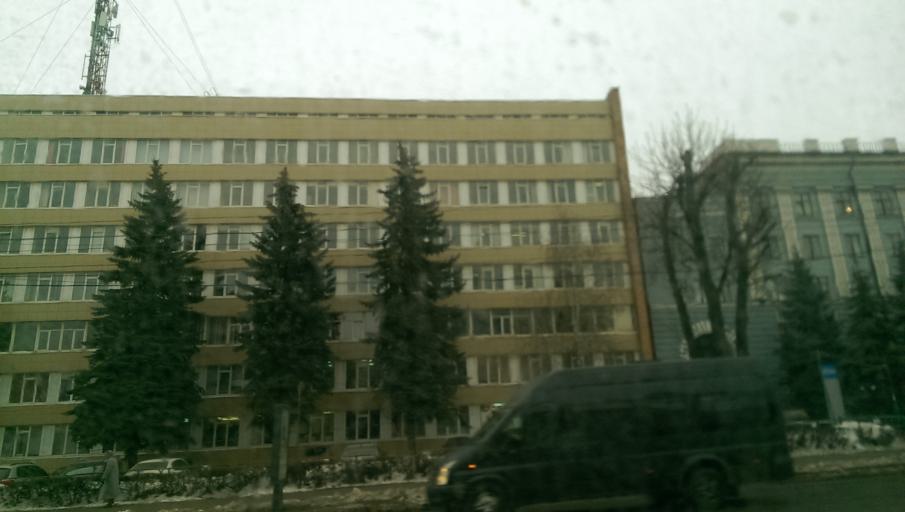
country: RU
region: Tula
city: Tula
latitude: 54.1799
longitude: 37.6033
